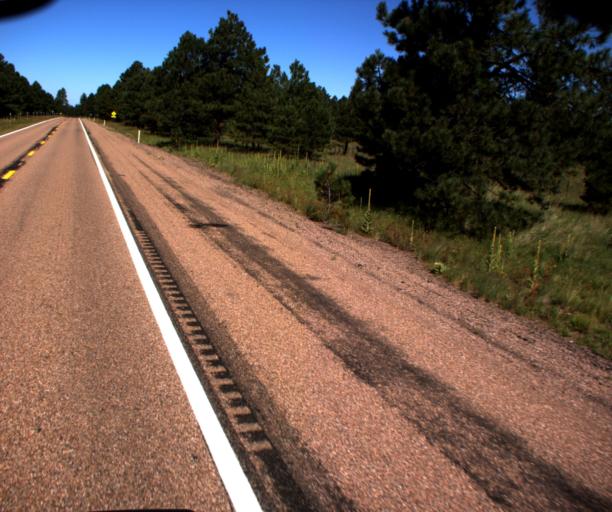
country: US
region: Arizona
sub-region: Navajo County
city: Pinetop-Lakeside
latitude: 34.0434
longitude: -109.6867
